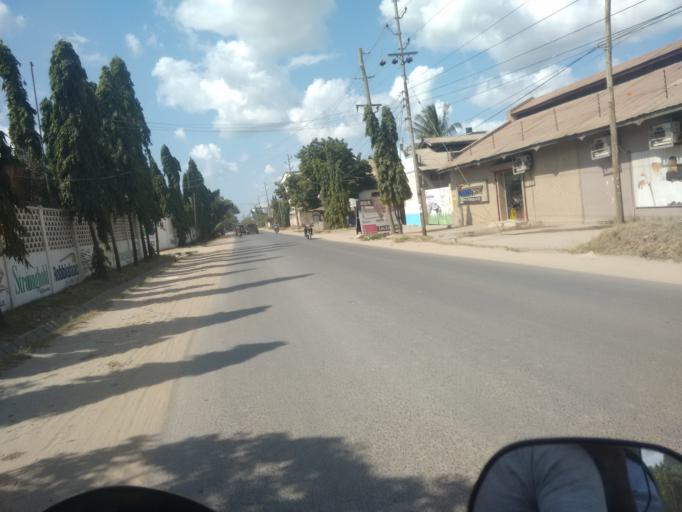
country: TZ
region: Dar es Salaam
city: Dar es Salaam
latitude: -6.8387
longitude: 39.2674
